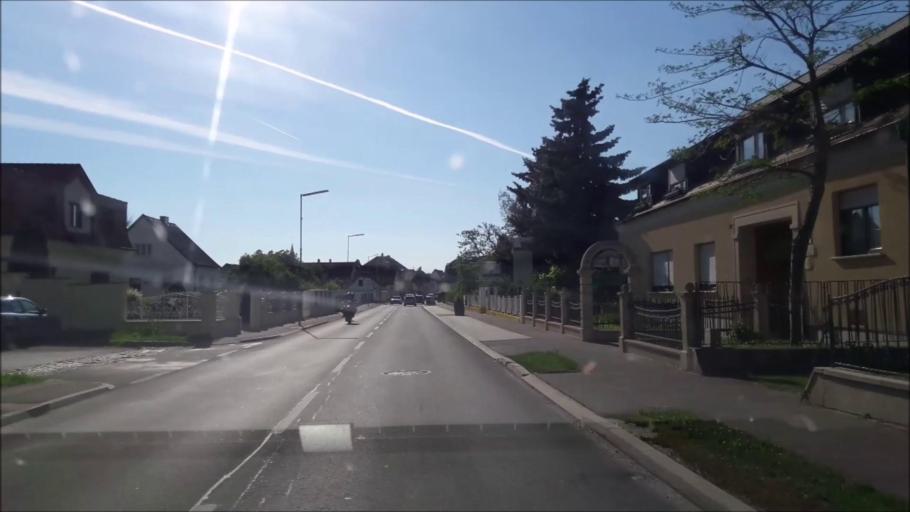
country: AT
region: Burgenland
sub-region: Eisenstadt-Umgebung
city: Sankt Margarethen im Burgenland
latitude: 47.8035
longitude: 16.6140
